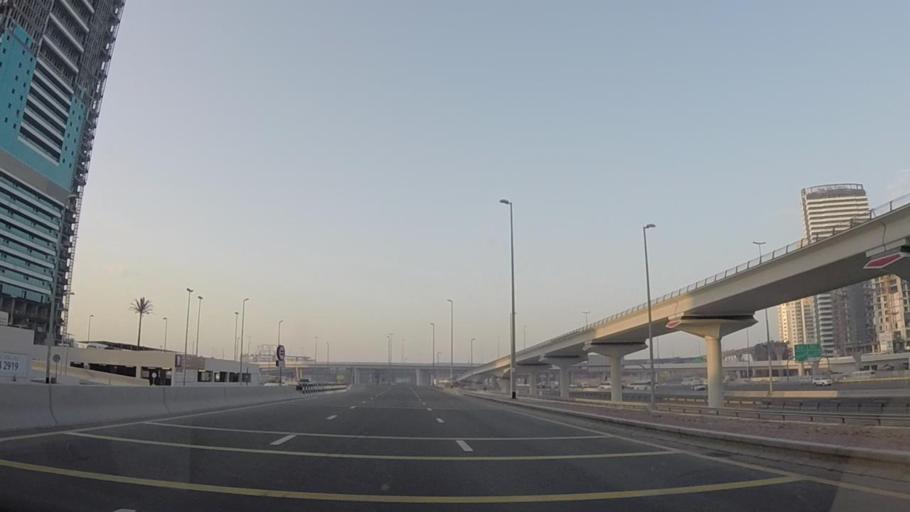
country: AE
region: Dubai
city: Dubai
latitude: 25.0689
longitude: 55.1375
